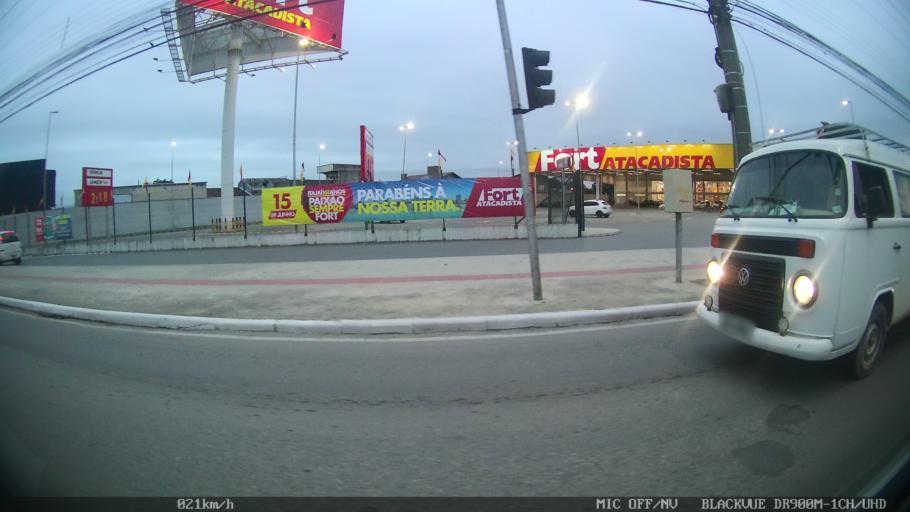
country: BR
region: Santa Catarina
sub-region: Itajai
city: Itajai
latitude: -26.8839
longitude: -48.6947
